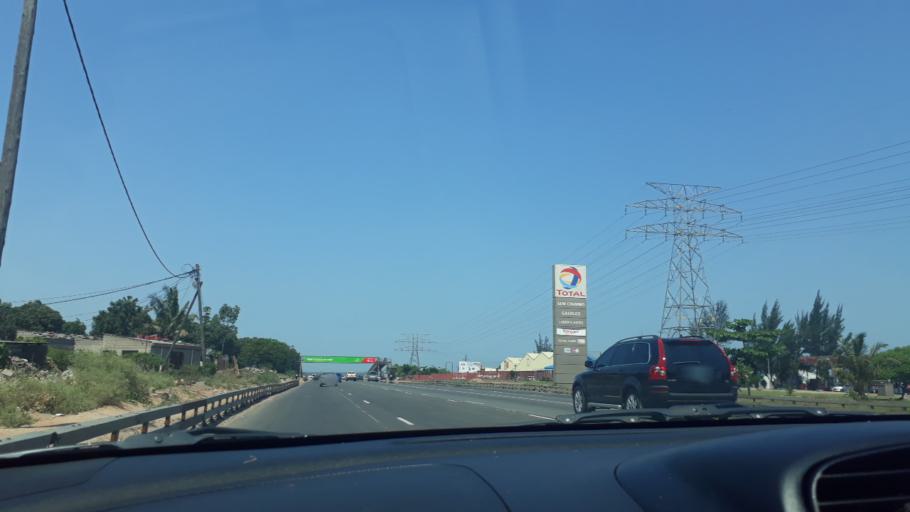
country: MZ
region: Maputo
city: Matola
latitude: -25.9344
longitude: 32.4999
